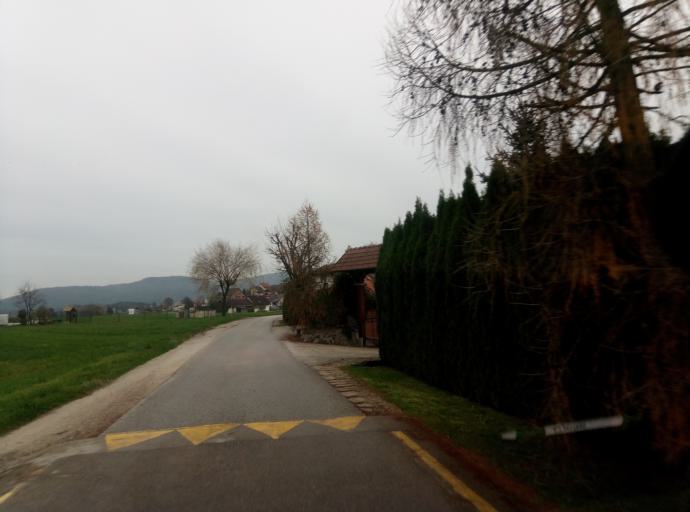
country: SI
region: Vodice
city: Vodice
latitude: 46.1802
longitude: 14.4795
